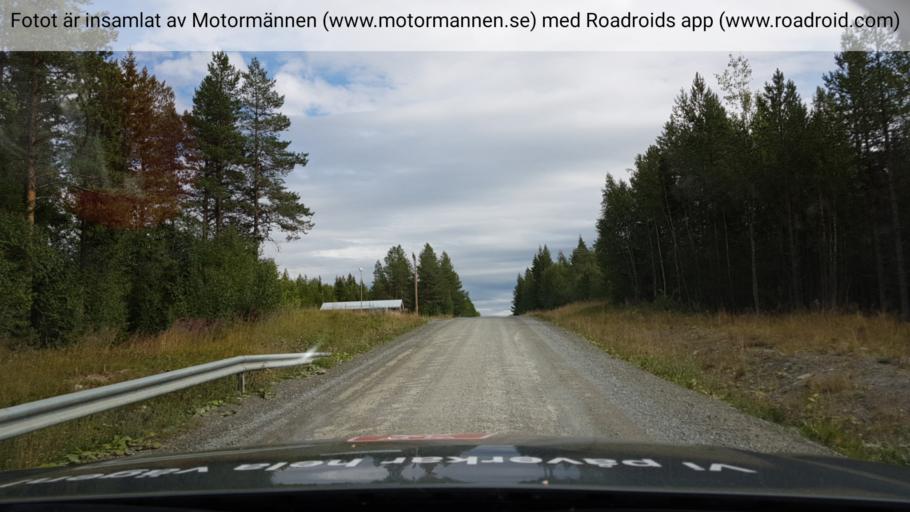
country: SE
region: Jaemtland
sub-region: Krokoms Kommun
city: Valla
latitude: 63.6469
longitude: 13.8179
